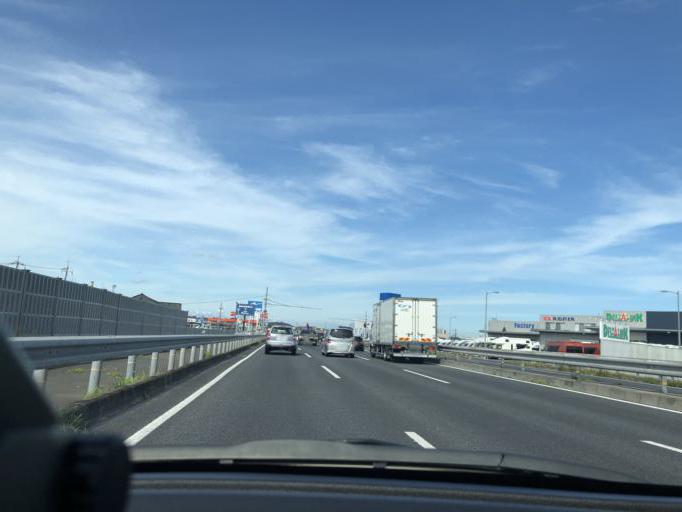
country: JP
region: Okayama
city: Kurashiki
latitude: 34.5923
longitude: 133.8002
